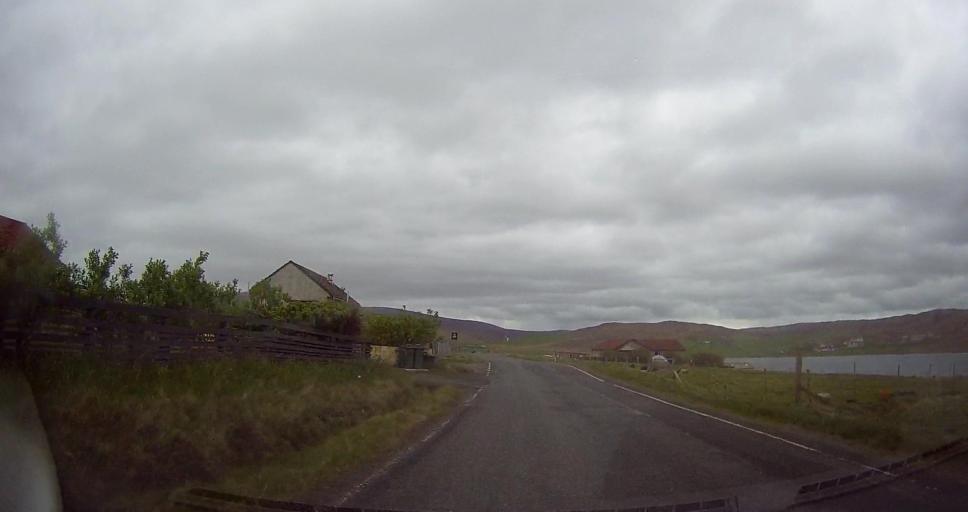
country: GB
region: Scotland
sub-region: Shetland Islands
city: Lerwick
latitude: 60.4849
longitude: -1.4699
